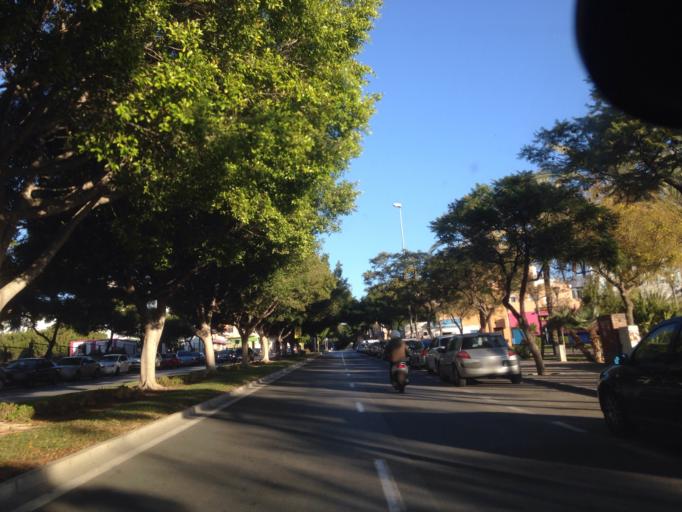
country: ES
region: Andalusia
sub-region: Provincia de Malaga
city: Malaga
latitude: 36.7194
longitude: -4.4712
